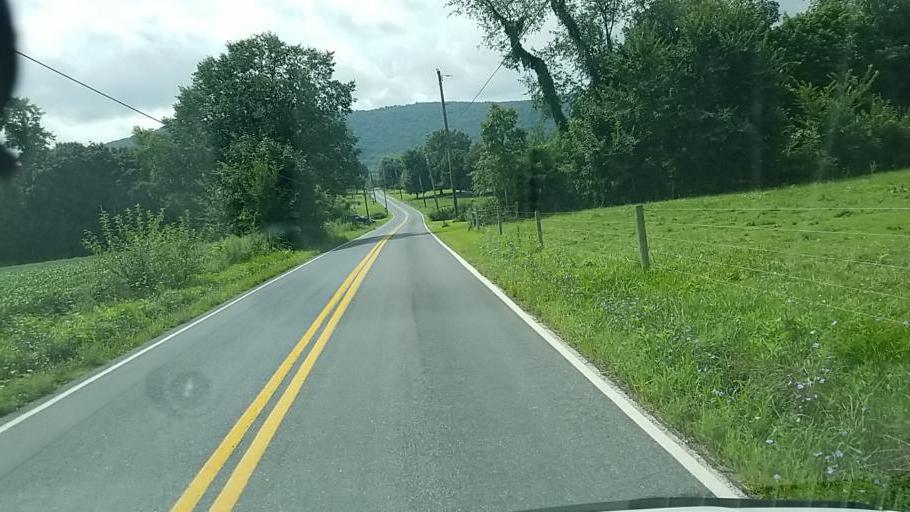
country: US
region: Pennsylvania
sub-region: Dauphin County
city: Millersburg
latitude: 40.5495
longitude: -76.8919
